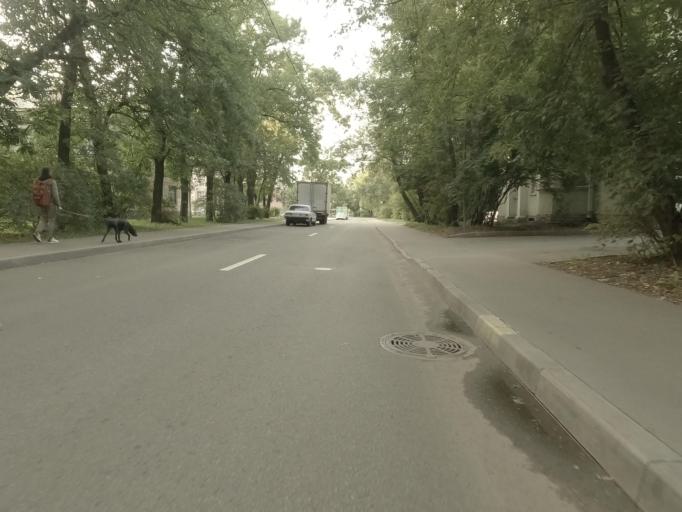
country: RU
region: St.-Petersburg
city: Admiralteisky
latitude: 59.8956
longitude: 30.2688
